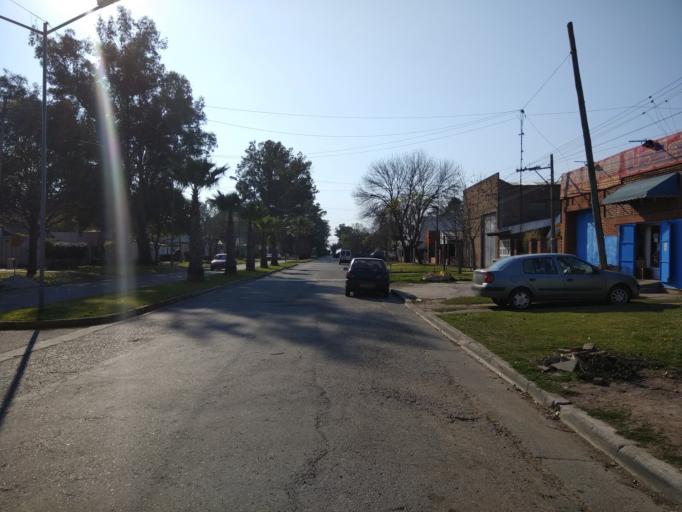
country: AR
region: Santa Fe
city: Granadero Baigorria
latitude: -32.8474
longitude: -60.7035
